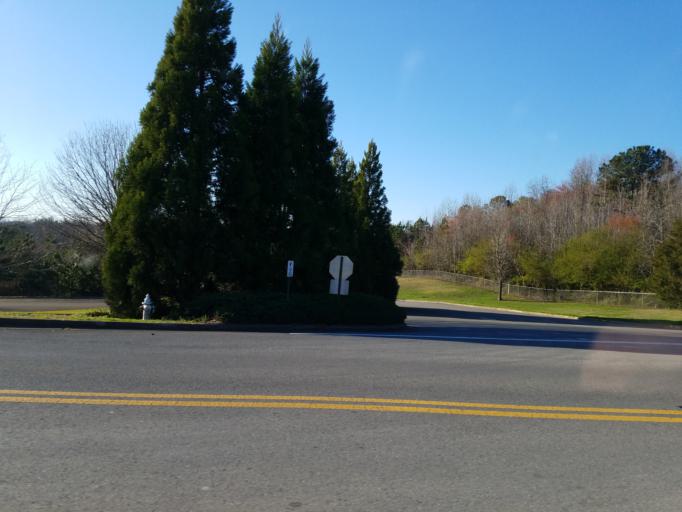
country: US
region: Georgia
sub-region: Pickens County
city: Jasper
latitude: 34.4336
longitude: -84.4285
